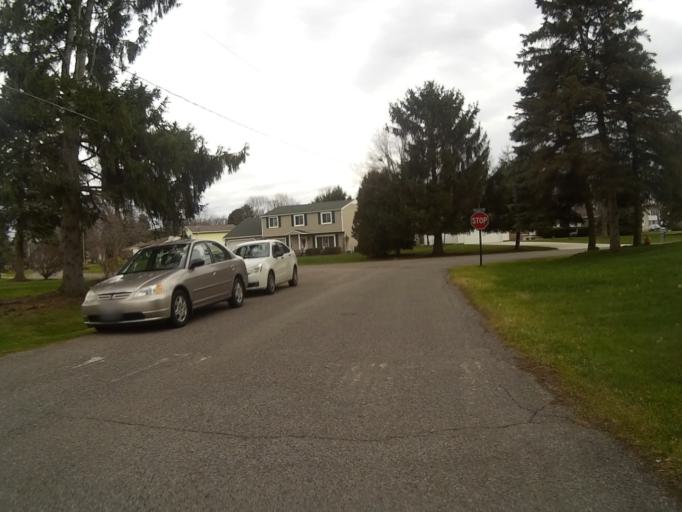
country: US
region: Ohio
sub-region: Stark County
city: Hartville
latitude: 41.0289
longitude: -81.3266
